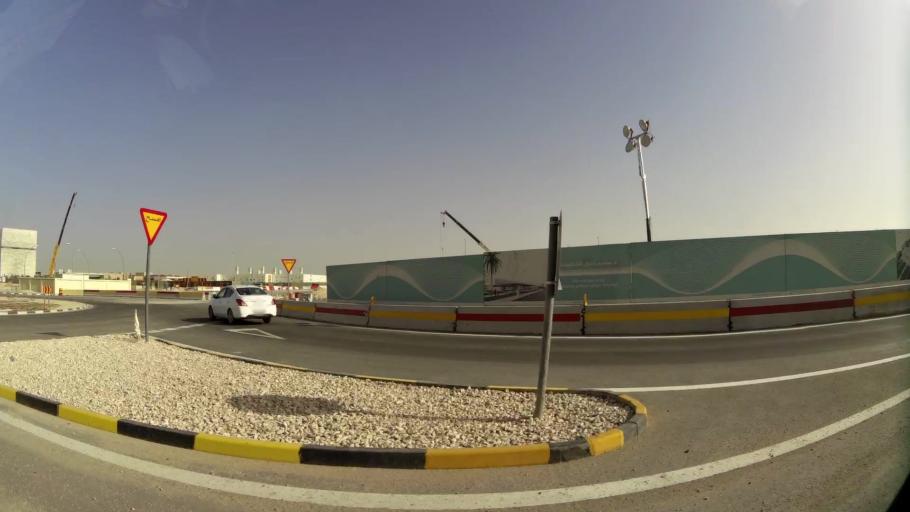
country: QA
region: Baladiyat ar Rayyan
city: Ar Rayyan
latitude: 25.3190
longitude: 51.4304
